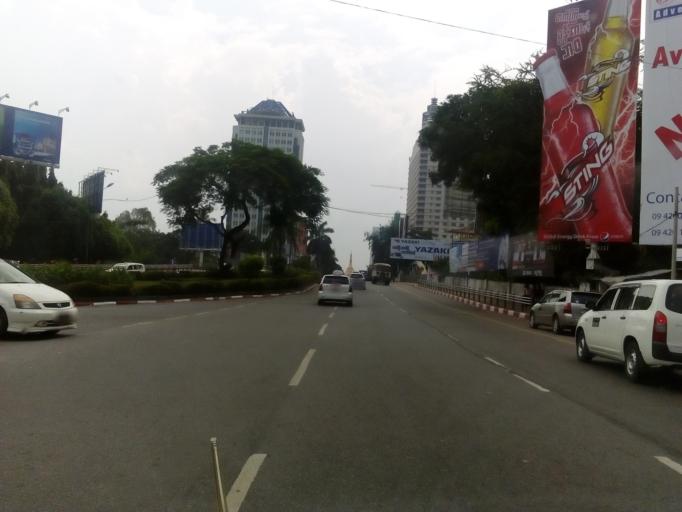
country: MM
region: Yangon
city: Yangon
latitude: 16.7822
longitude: 96.1591
